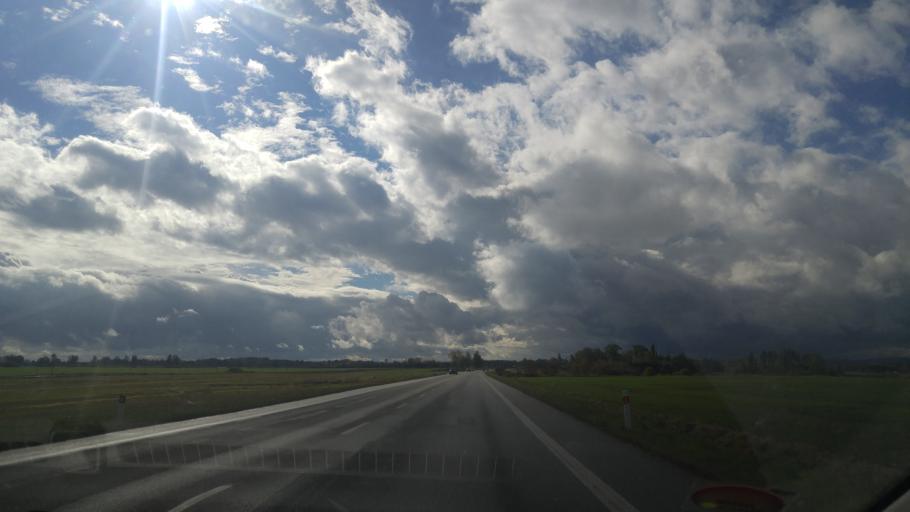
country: CZ
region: Jihocesky
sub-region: Okres Tabor
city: Veseli nad Luznici
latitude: 49.1785
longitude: 14.6902
